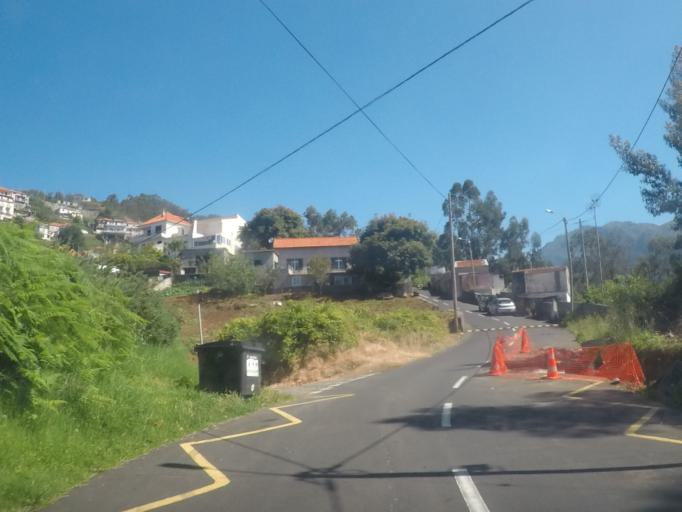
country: PT
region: Madeira
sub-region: Camara de Lobos
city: Curral das Freiras
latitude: 32.6803
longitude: -16.9672
